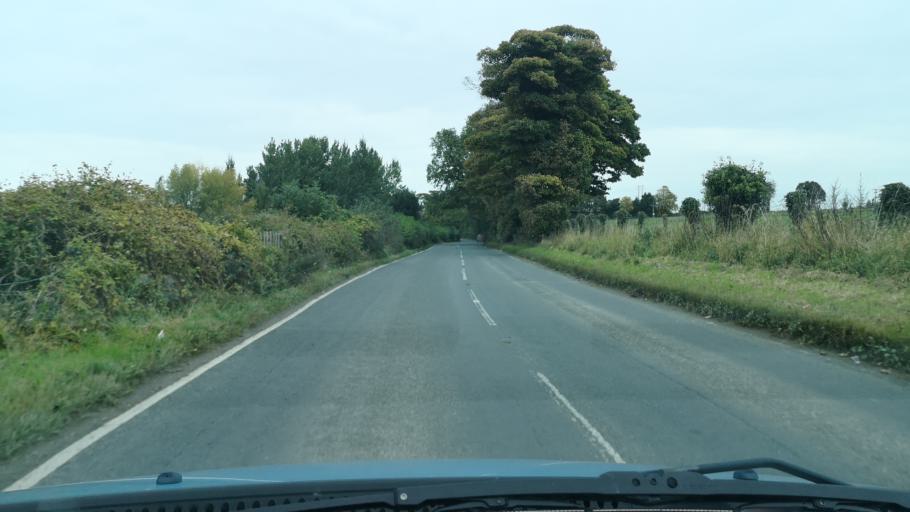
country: GB
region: England
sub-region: City and Borough of Wakefield
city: Fitzwilliam
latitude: 53.6388
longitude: -1.3798
